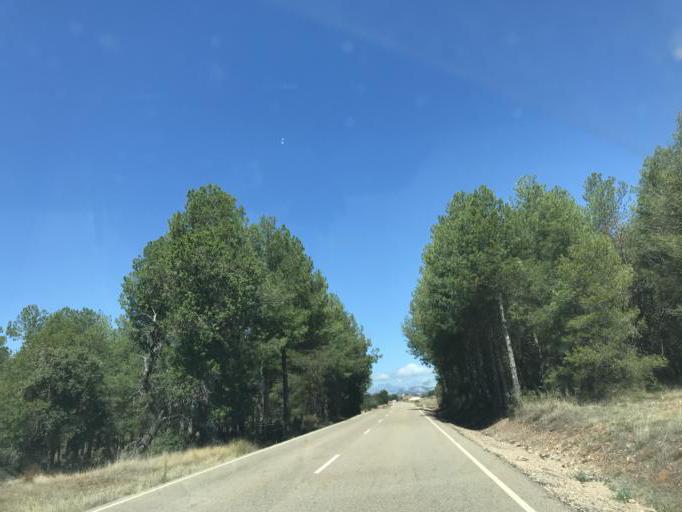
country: ES
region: Castille and Leon
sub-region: Provincia de Palencia
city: Olmos de Ojeda
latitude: 42.6979
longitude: -4.4061
